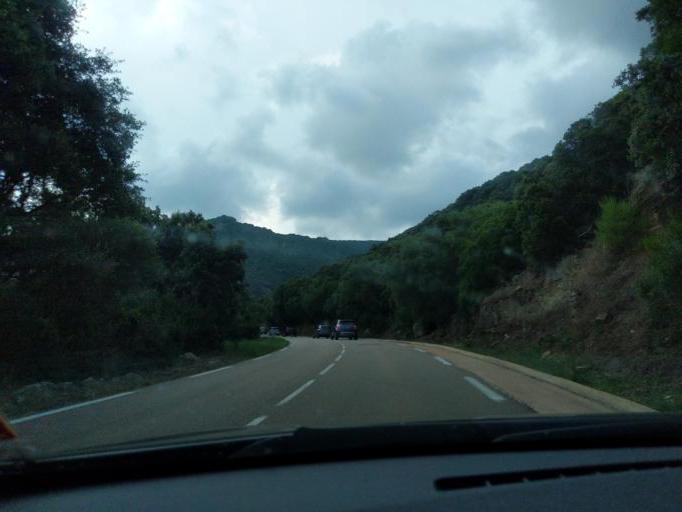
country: FR
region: Corsica
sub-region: Departement de la Corse-du-Sud
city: Sartene
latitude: 41.5772
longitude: 8.9520
